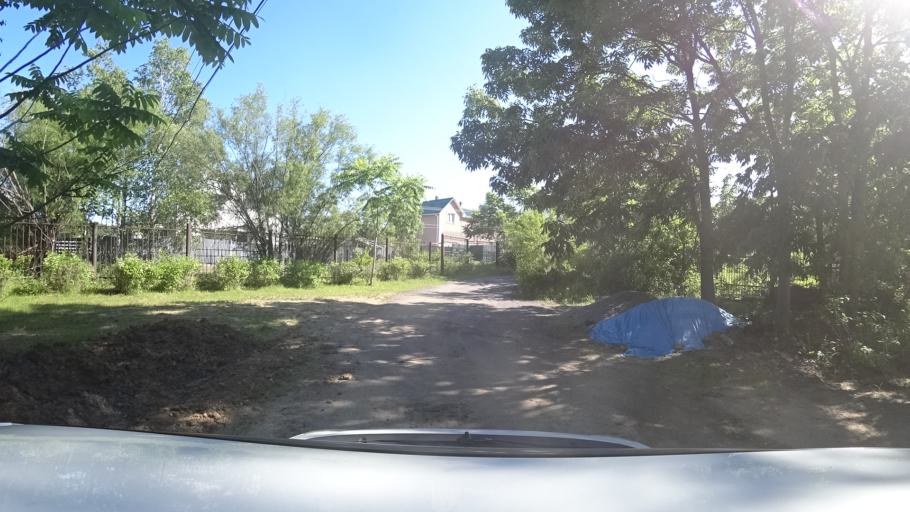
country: RU
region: Khabarovsk Krai
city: Topolevo
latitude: 48.5466
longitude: 135.1794
